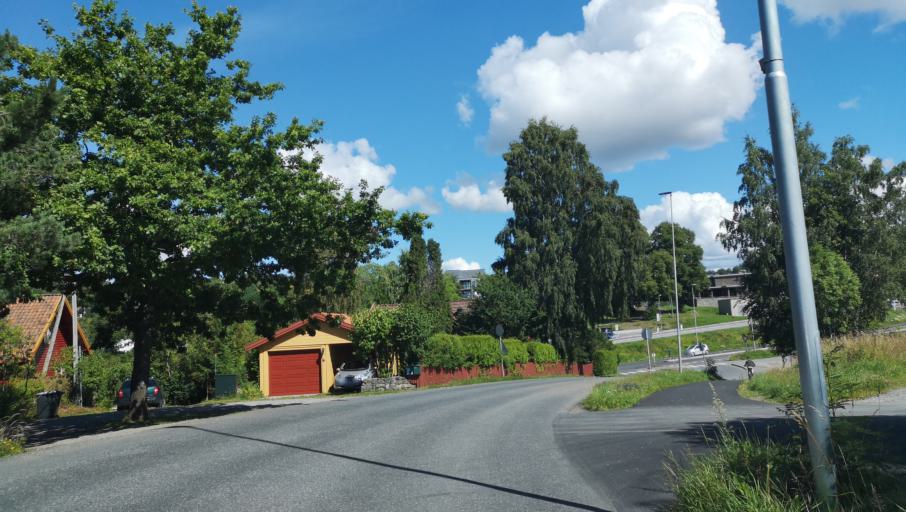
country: NO
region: Akershus
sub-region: Frogn
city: Drobak
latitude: 59.6660
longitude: 10.6412
